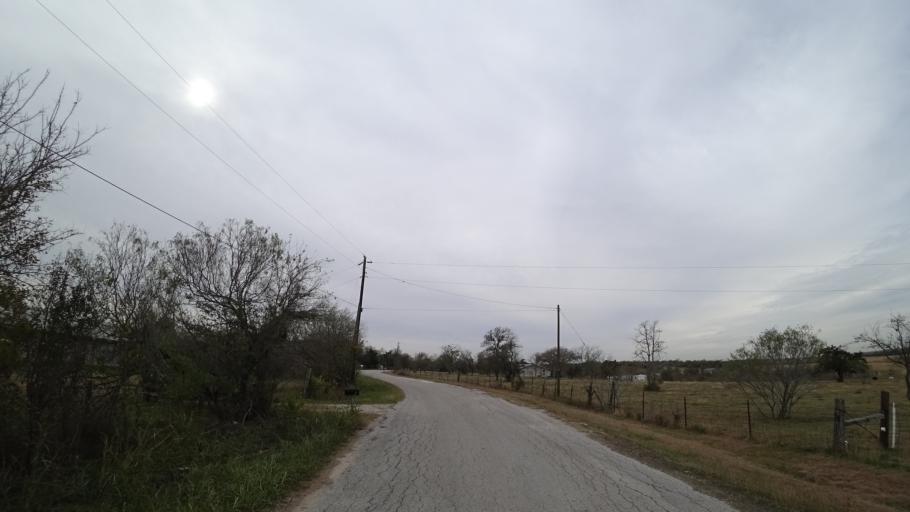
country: US
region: Texas
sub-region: Travis County
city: Garfield
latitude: 30.1221
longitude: -97.5610
